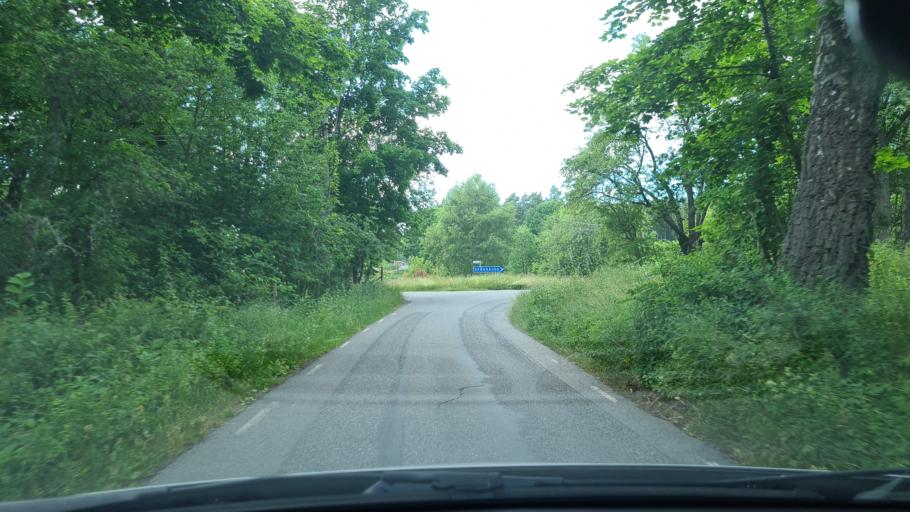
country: SE
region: Stockholm
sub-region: Vaxholms Kommun
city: Vaxholm
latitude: 59.4139
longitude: 18.4378
